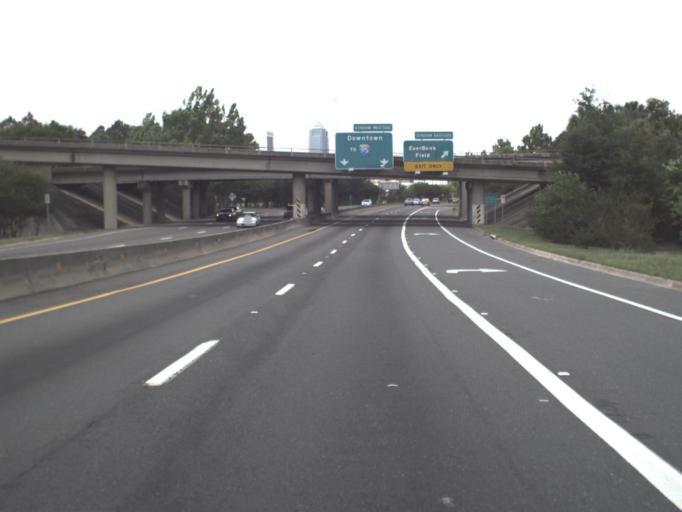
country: US
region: Florida
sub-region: Duval County
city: Jacksonville
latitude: 30.3272
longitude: -81.6354
